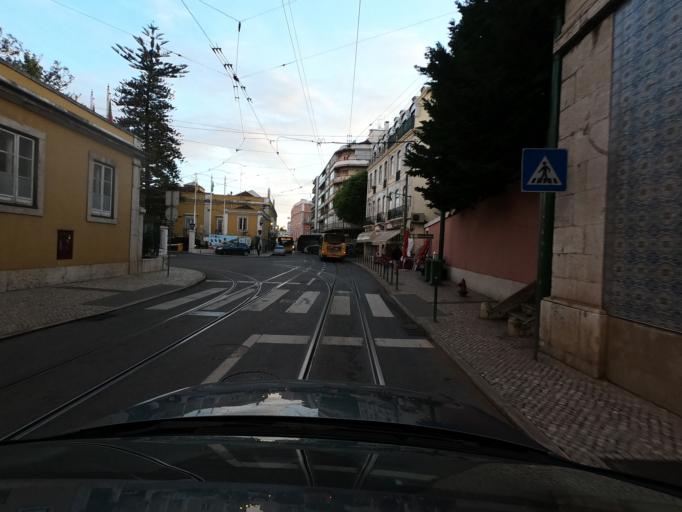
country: PT
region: Setubal
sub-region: Almada
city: Pragal
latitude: 38.7027
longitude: -9.1803
